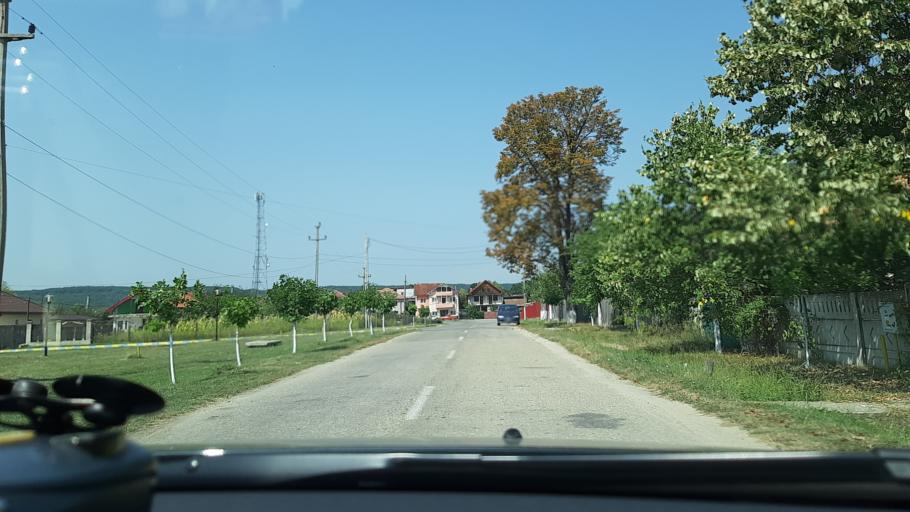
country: RO
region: Gorj
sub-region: Comuna Targu Carbunesti
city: Targu Carbunesti
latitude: 44.9638
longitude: 23.5171
